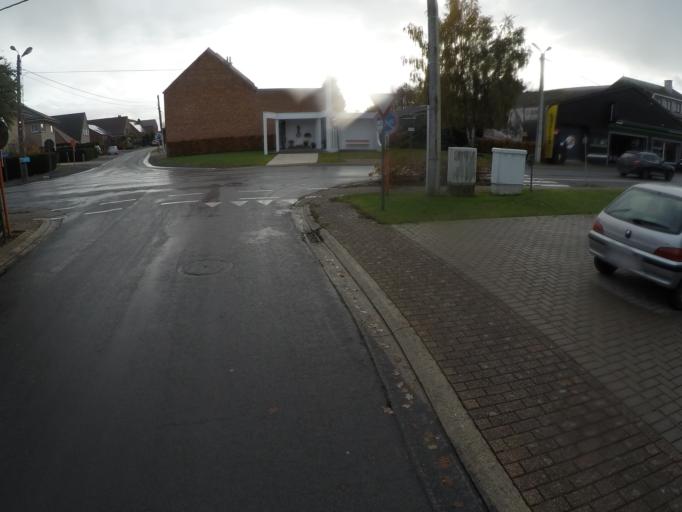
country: BE
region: Flanders
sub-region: Provincie Vlaams-Brabant
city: Opwijk
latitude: 50.9653
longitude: 4.1918
